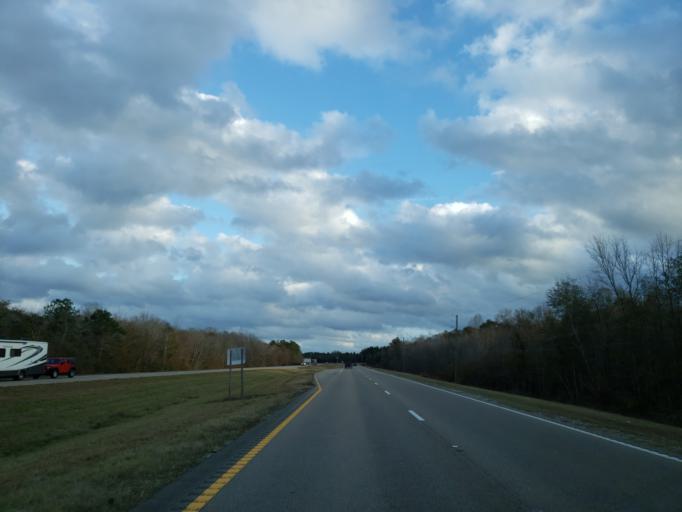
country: US
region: Mississippi
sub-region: Perry County
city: New Augusta
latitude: 31.1488
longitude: -88.8869
